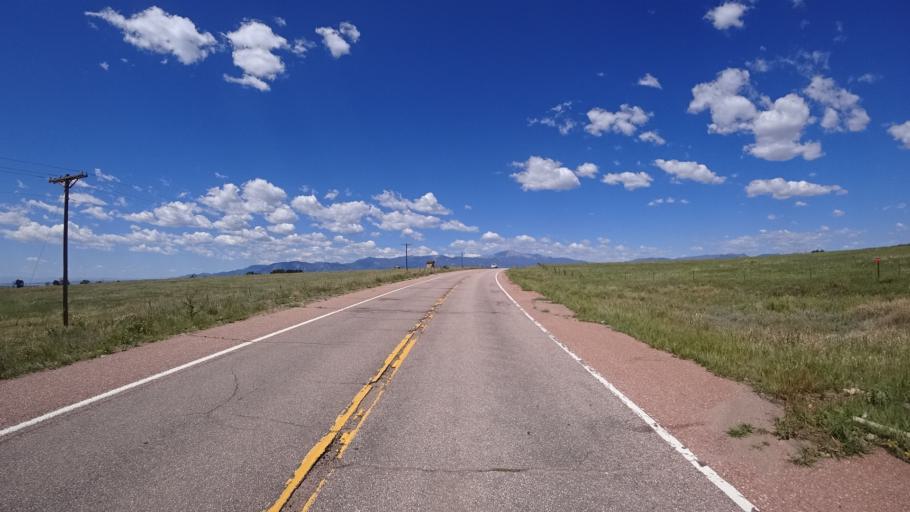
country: US
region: Colorado
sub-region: El Paso County
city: Cimarron Hills
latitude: 38.8375
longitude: -104.6767
